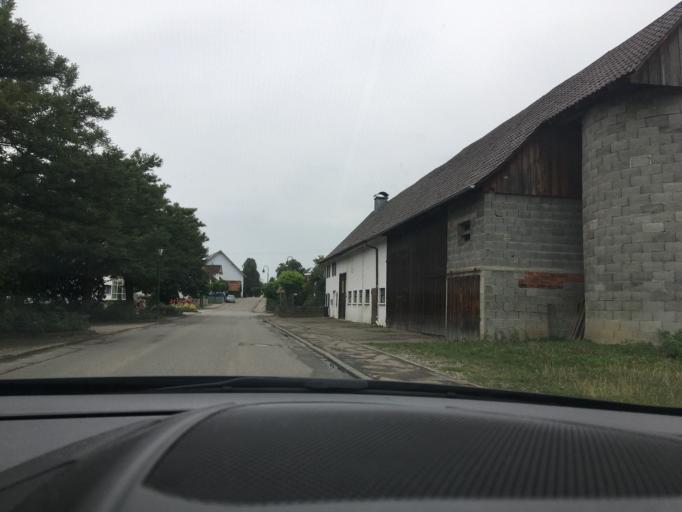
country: DE
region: Baden-Wuerttemberg
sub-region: Tuebingen Region
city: Kirchdorf
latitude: 48.0784
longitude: 10.1281
